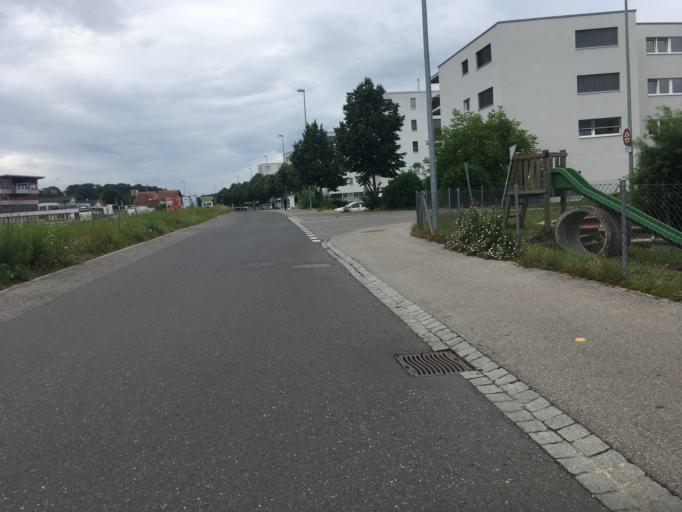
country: CH
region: Fribourg
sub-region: See District
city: Murten
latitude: 46.9204
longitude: 7.1086
